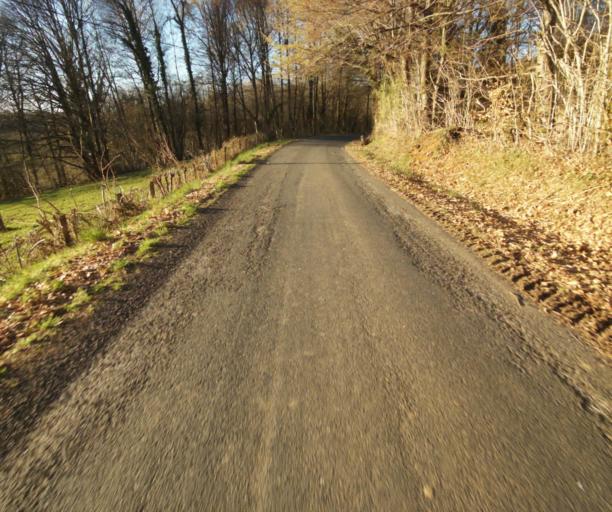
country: FR
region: Limousin
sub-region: Departement de la Correze
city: Seilhac
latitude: 45.3539
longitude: 1.7056
